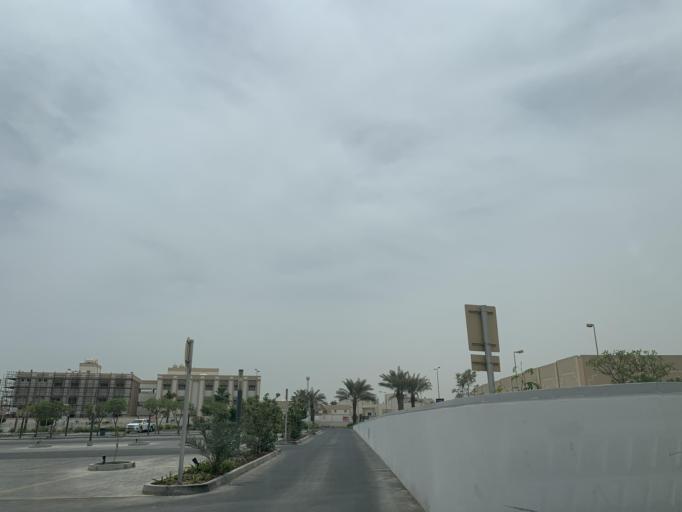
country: BH
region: Northern
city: Ar Rifa'
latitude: 26.1369
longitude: 50.5583
